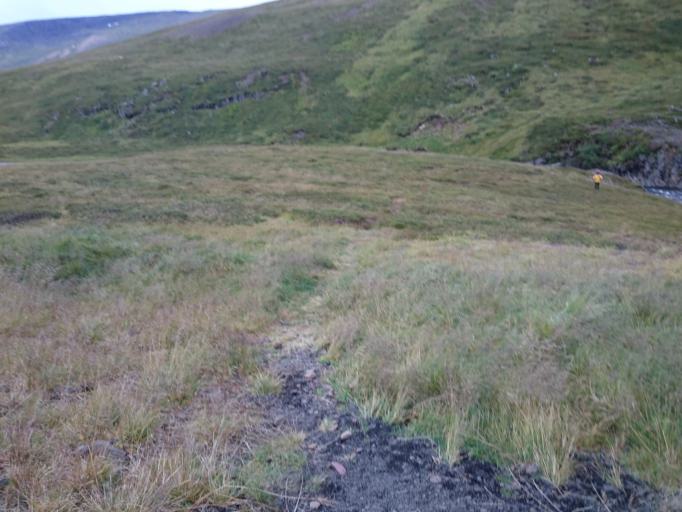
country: IS
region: West
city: Borgarnes
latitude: 65.2617
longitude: -21.7612
